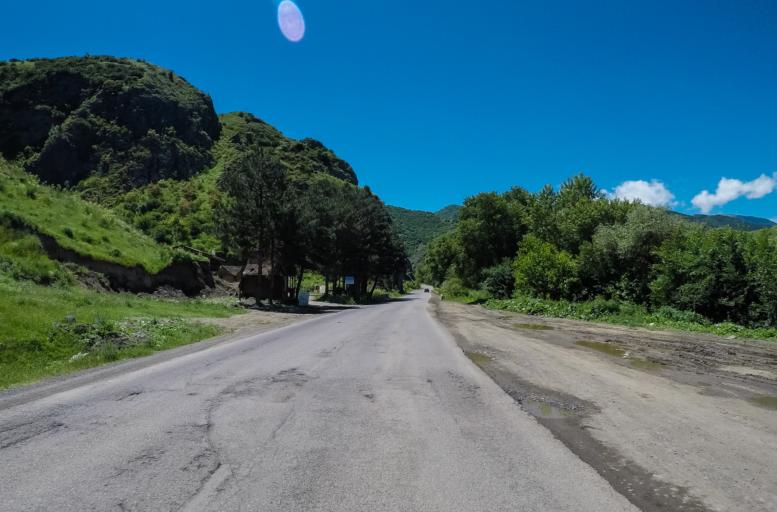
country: GE
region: Samtskhe-Javakheti
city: Akhaltsikhe
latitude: 41.6267
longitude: 43.0514
